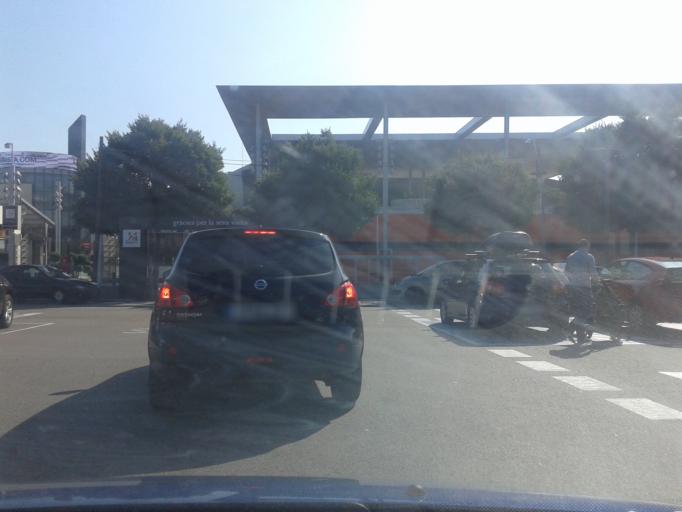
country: ES
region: Catalonia
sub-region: Provincia de Barcelona
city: Sant Andreu de Palomar
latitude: 41.4398
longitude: 2.1965
